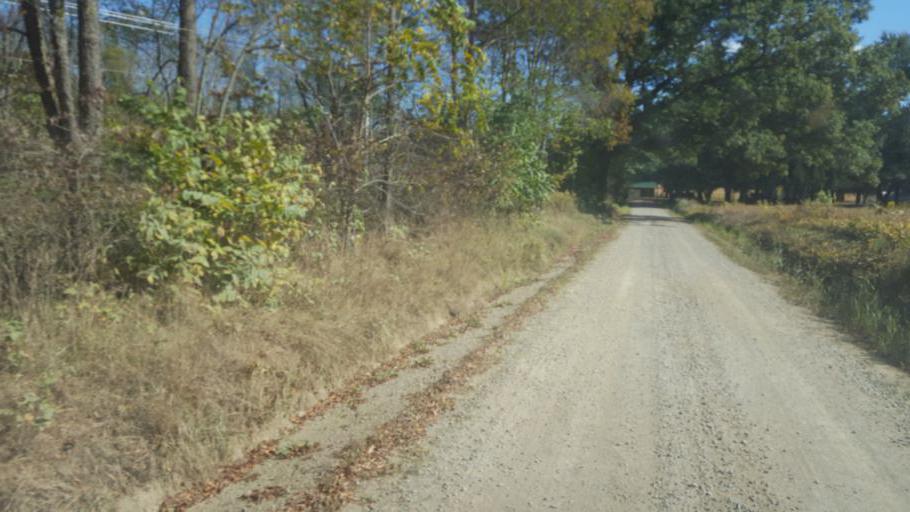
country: US
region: Pennsylvania
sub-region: Mercer County
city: Mercer
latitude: 41.3276
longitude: -80.2510
